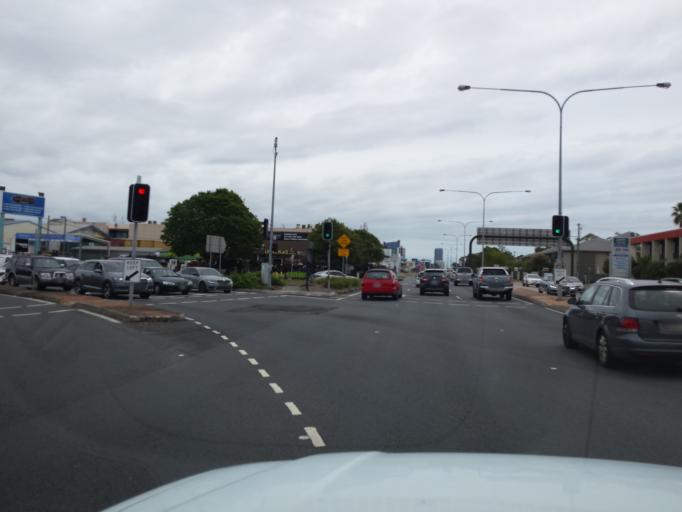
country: AU
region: Queensland
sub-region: Gold Coast
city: Surfers Paradise
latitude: -28.0117
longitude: 153.4118
